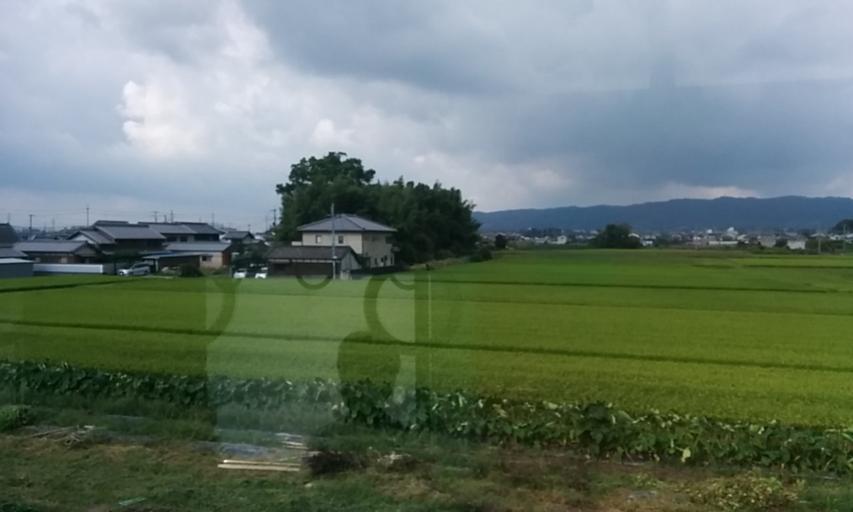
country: JP
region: Nara
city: Nara-shi
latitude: 34.6346
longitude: 135.7806
